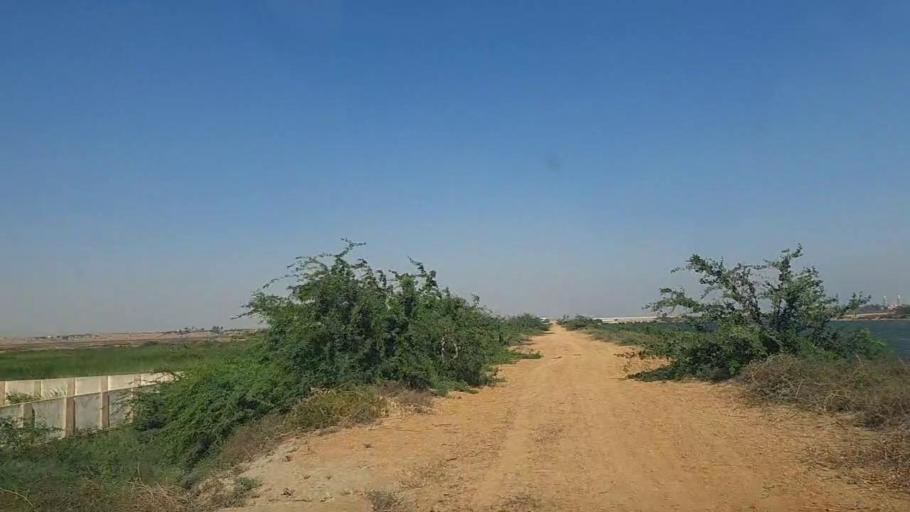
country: PK
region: Sindh
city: Thatta
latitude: 24.8216
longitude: 67.9901
